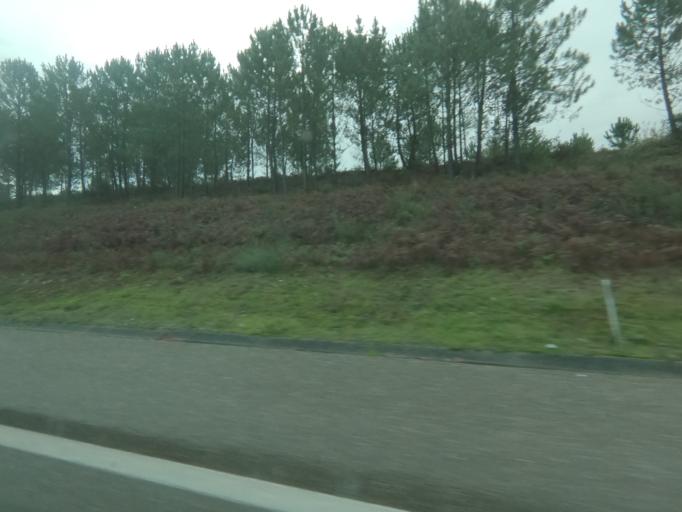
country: PT
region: Viana do Castelo
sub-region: Valenca
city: Valenza
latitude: 41.9803
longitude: -8.6520
